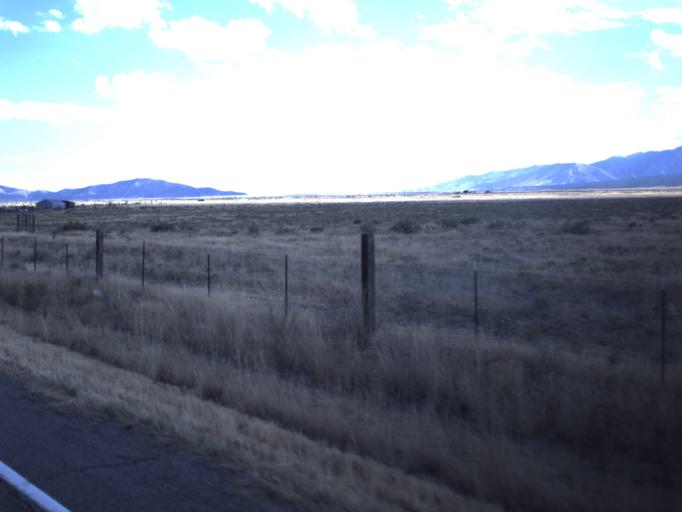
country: US
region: Utah
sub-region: Tooele County
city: Grantsville
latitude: 40.6135
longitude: -112.4960
